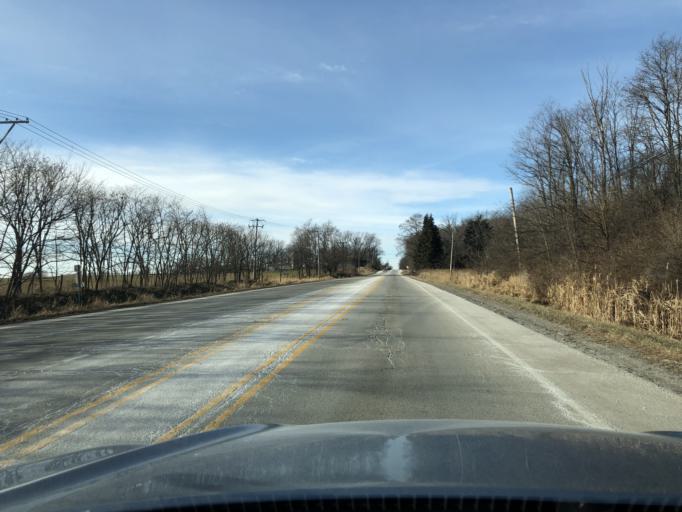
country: US
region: Illinois
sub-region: Lake County
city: Wadsworth
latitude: 42.4658
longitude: -87.9734
